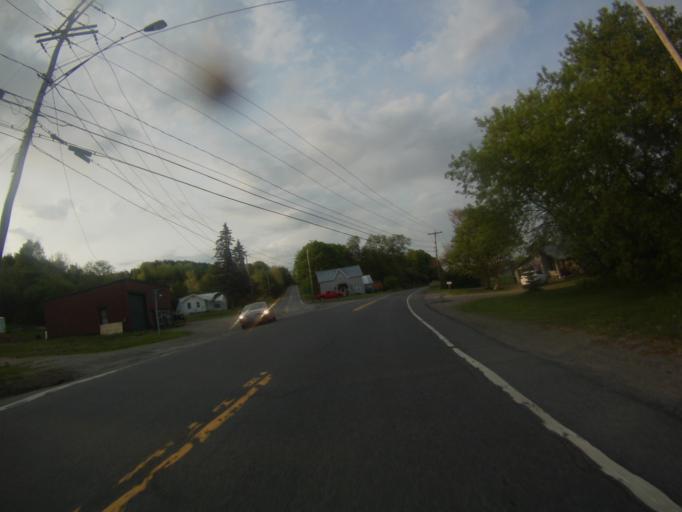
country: US
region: New York
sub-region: Essex County
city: Ticonderoga
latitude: 43.8851
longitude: -73.4482
